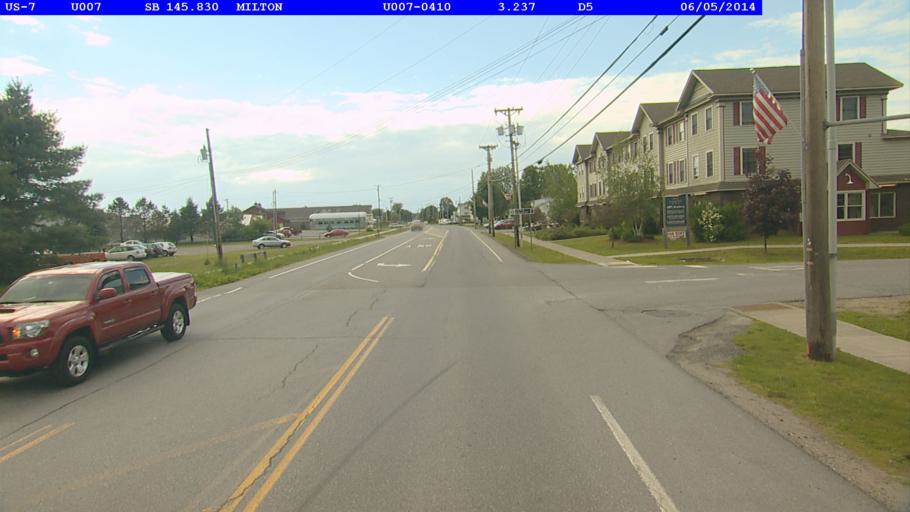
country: US
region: Vermont
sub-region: Chittenden County
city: Milton
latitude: 44.6227
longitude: -73.1305
